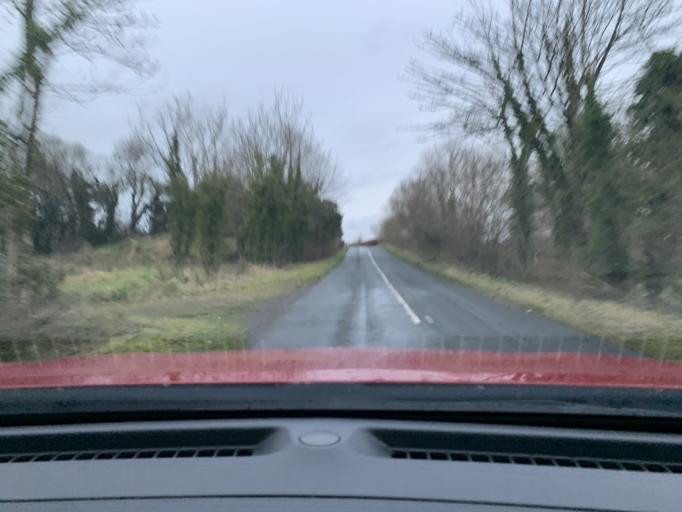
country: IE
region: Connaught
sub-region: Roscommon
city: Boyle
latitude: 54.0366
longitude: -8.3341
